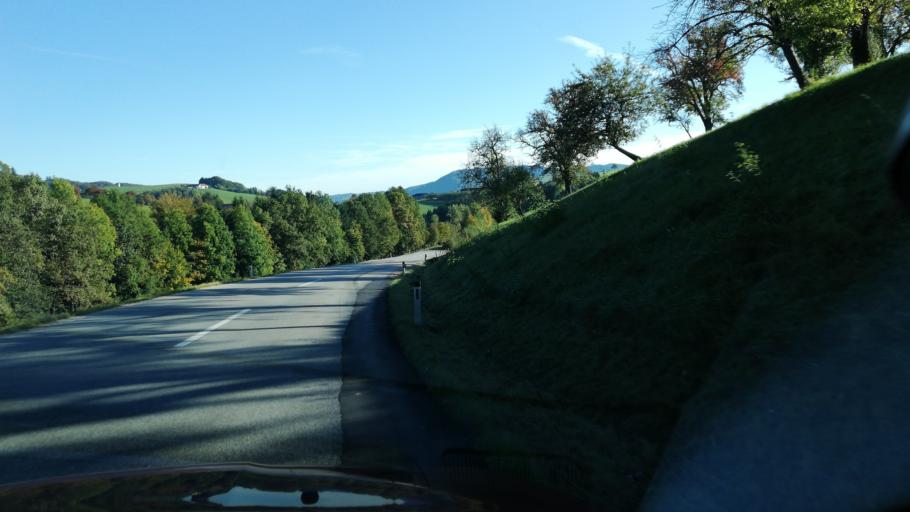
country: AT
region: Upper Austria
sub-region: Politischer Bezirk Steyr-Land
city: Ternberg
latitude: 47.9652
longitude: 14.3249
